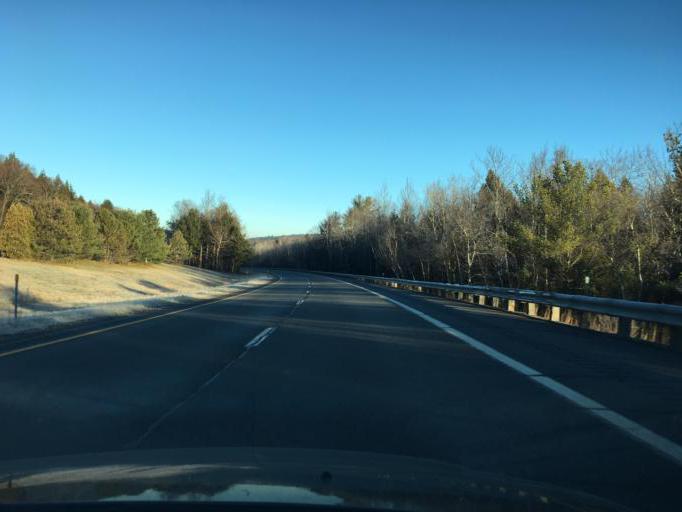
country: US
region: New Hampshire
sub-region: Belknap County
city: Sanbornton
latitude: 43.5601
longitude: -71.6169
